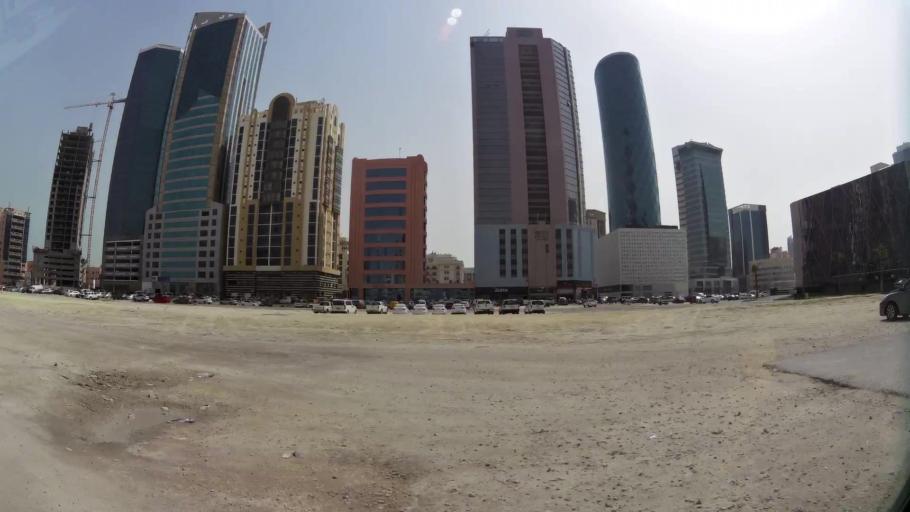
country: BH
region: Manama
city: Jidd Hafs
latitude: 26.2397
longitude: 50.5347
